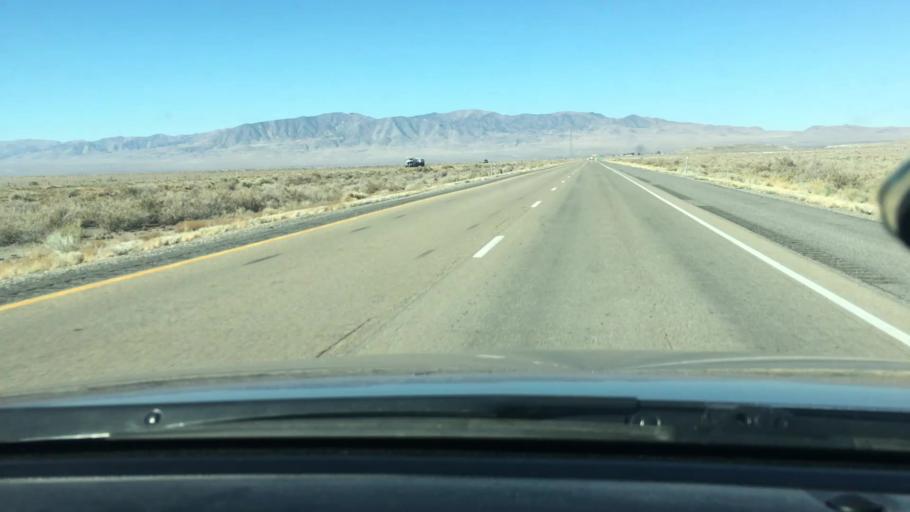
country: US
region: Utah
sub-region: Tooele County
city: Grantsville
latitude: 40.7548
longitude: -112.7401
